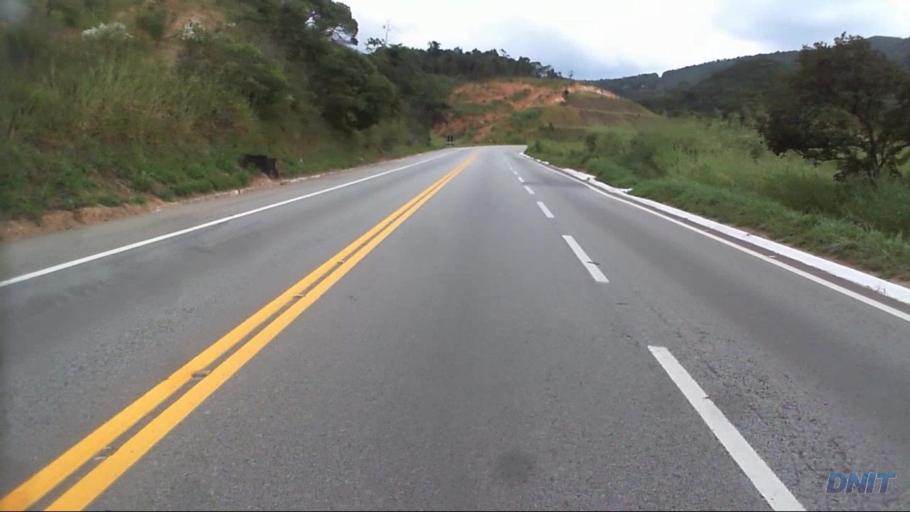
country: BR
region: Minas Gerais
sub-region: Caete
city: Caete
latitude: -19.7952
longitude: -43.6752
